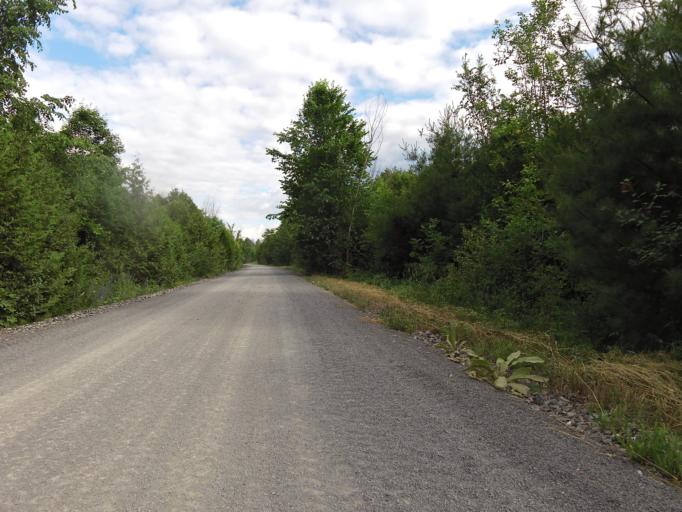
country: CA
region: Ontario
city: Arnprior
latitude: 45.2966
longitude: -76.2619
